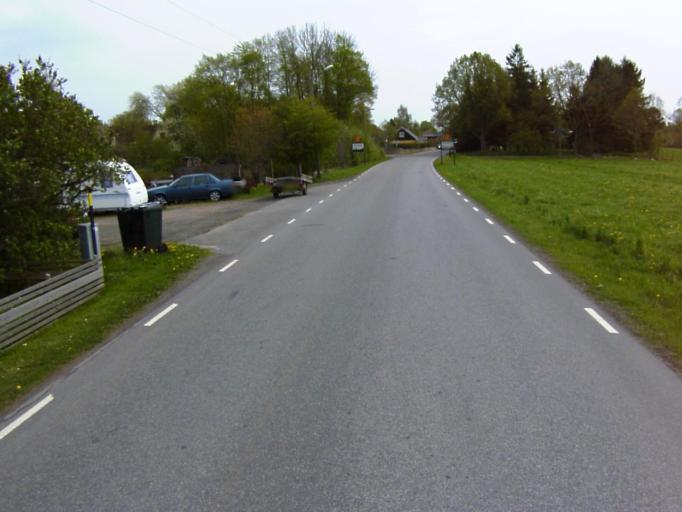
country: SE
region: Skane
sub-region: Kristianstads Kommun
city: Onnestad
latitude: 55.9390
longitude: 13.9536
